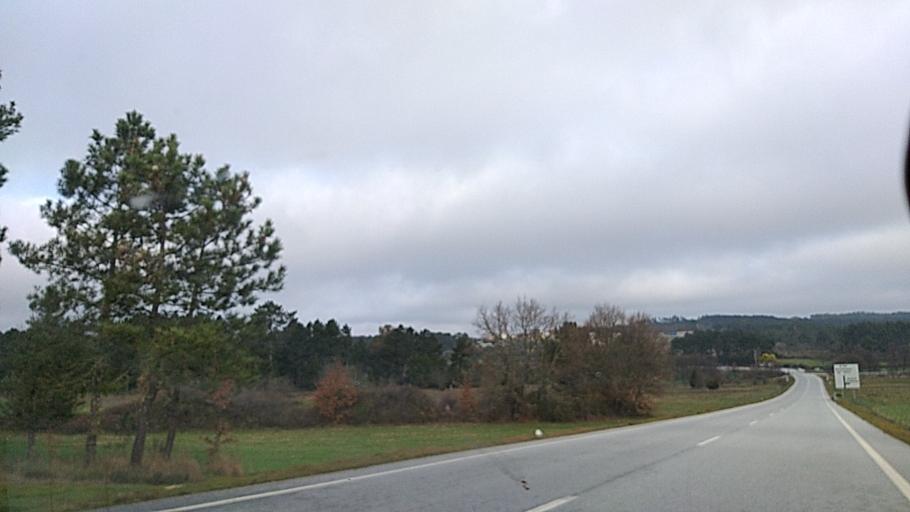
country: PT
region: Guarda
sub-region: Fornos de Algodres
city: Fornos de Algodres
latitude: 40.7149
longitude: -7.4869
